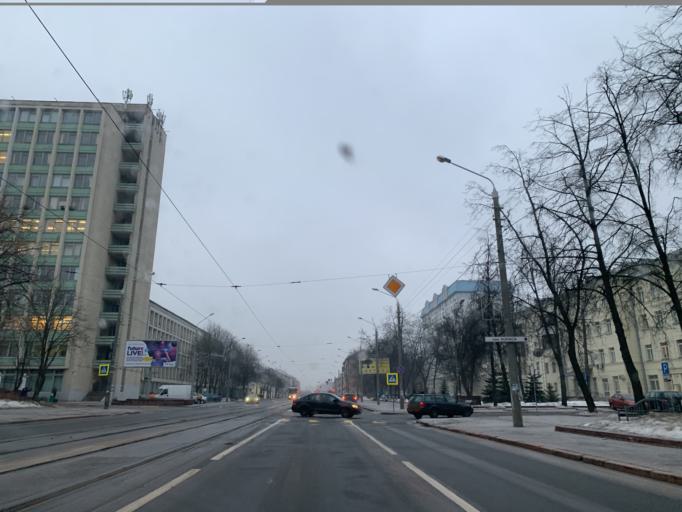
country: BY
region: Minsk
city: Minsk
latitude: 53.9220
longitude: 27.5895
